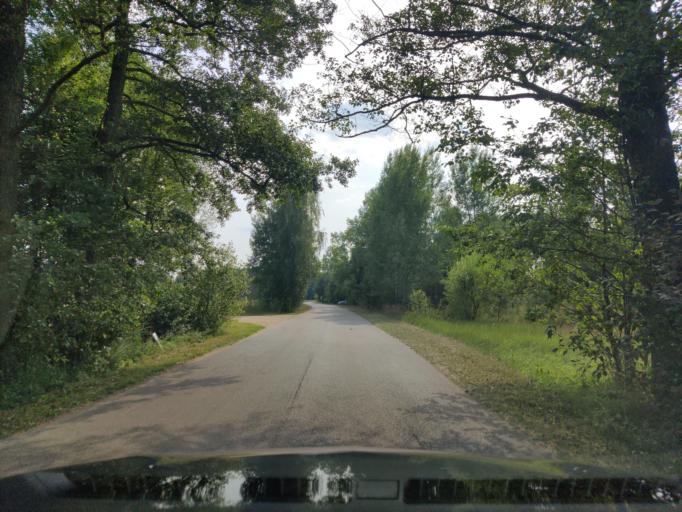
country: PL
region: Masovian Voivodeship
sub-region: Powiat wyszkowski
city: Rzasnik
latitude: 52.7664
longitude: 21.4573
